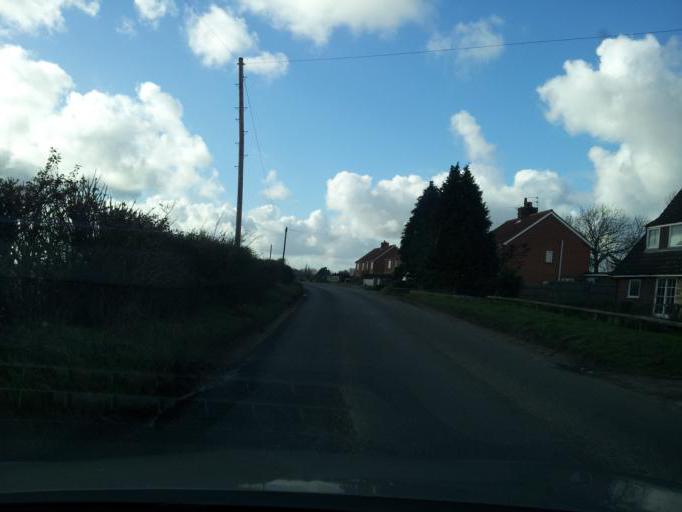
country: GB
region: England
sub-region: Norfolk
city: Mattishall
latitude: 52.6593
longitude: 1.0476
